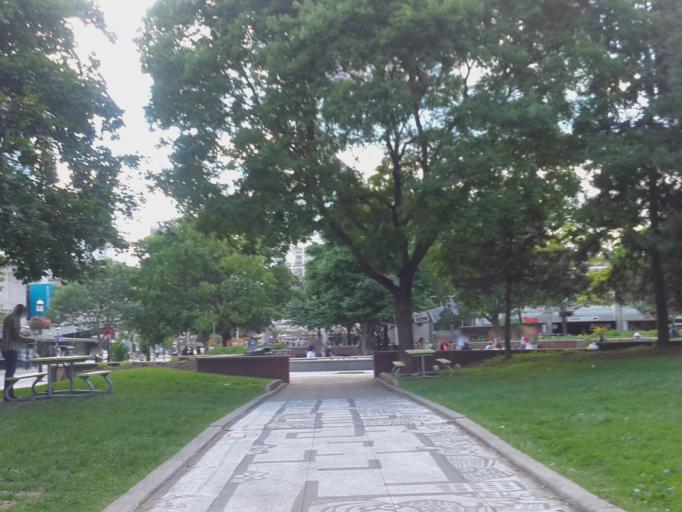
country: CA
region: Ontario
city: Toronto
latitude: 43.6482
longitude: -79.3746
